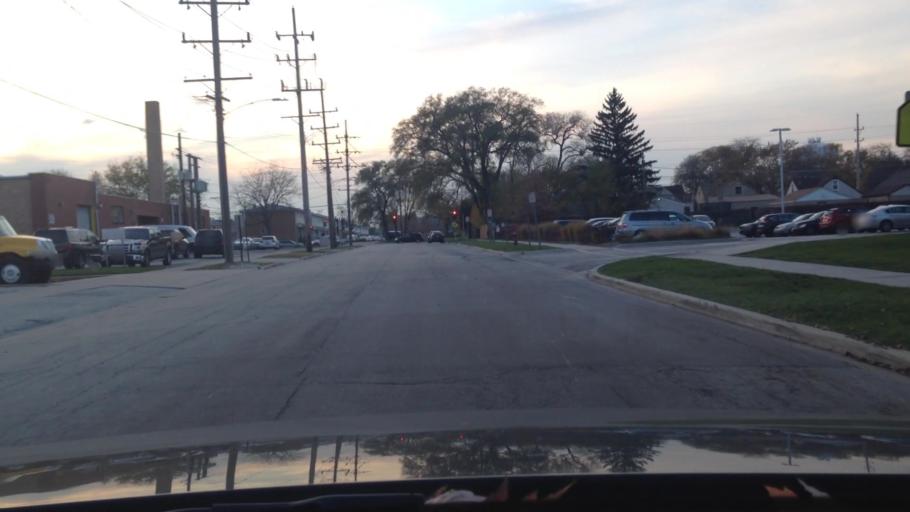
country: US
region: Illinois
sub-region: Cook County
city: Schiller Park
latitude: 41.9512
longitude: -87.8692
